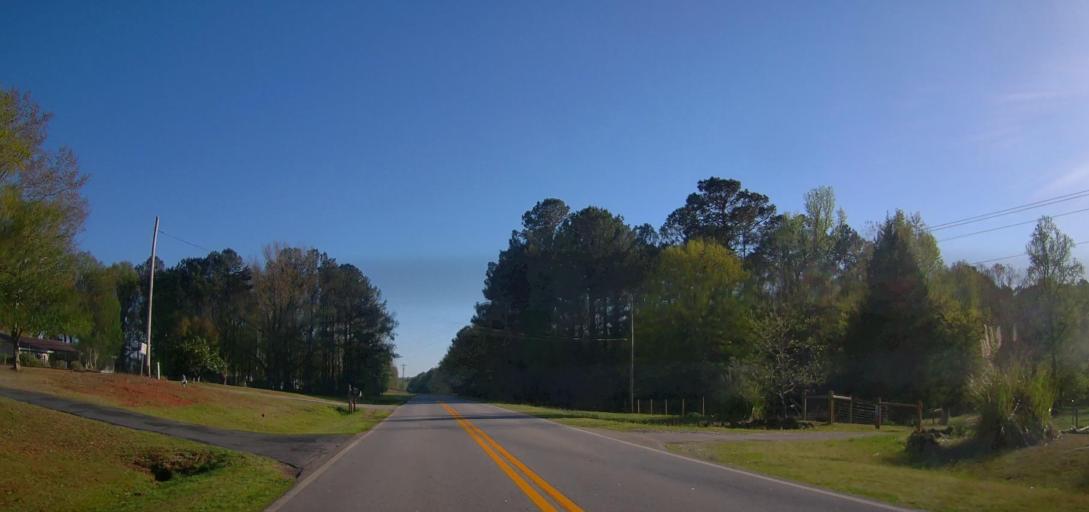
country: US
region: Georgia
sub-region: Butts County
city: Jackson
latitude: 33.3214
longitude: -83.9023
